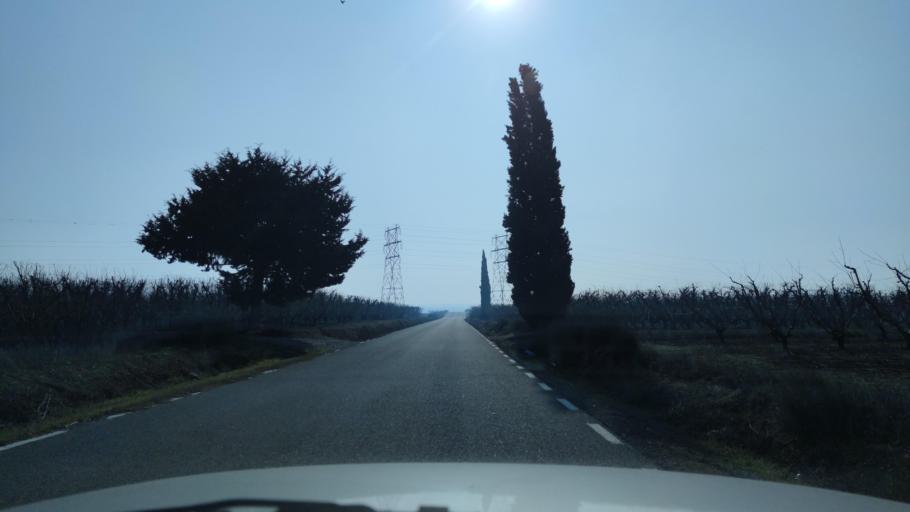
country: ES
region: Catalonia
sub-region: Provincia de Lleida
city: Sunyer
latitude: 41.5491
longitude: 0.5746
